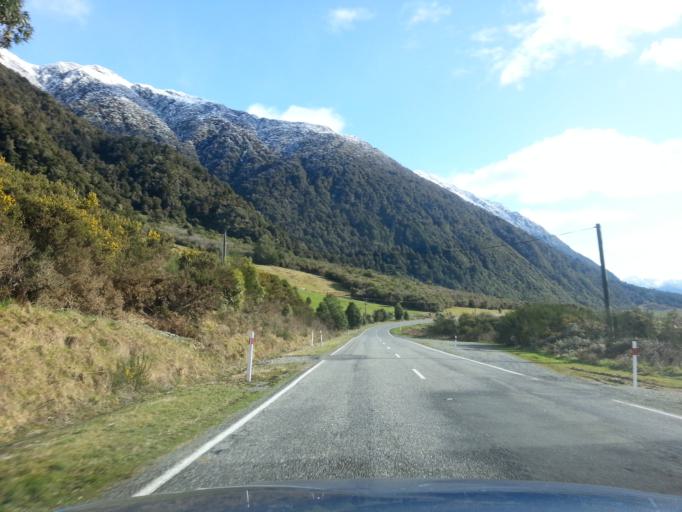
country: NZ
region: West Coast
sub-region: Grey District
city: Greymouth
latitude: -42.7593
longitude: 171.5695
